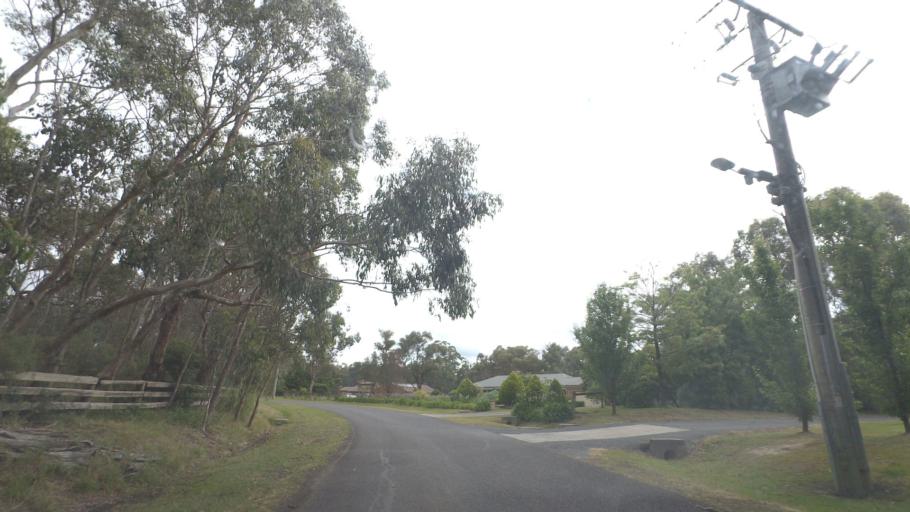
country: AU
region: Victoria
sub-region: Maroondah
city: Kilsyth South
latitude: -37.8240
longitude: 145.3103
